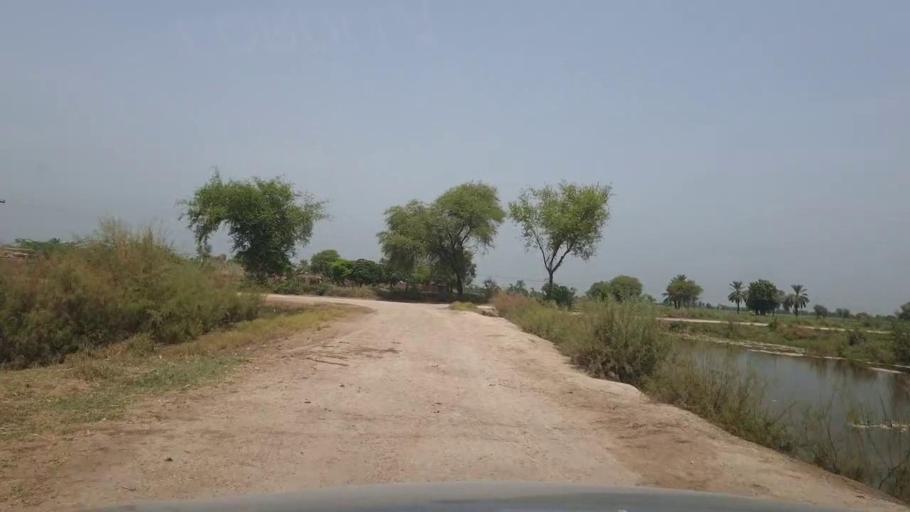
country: PK
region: Sindh
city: Garhi Yasin
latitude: 27.9219
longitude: 68.3753
